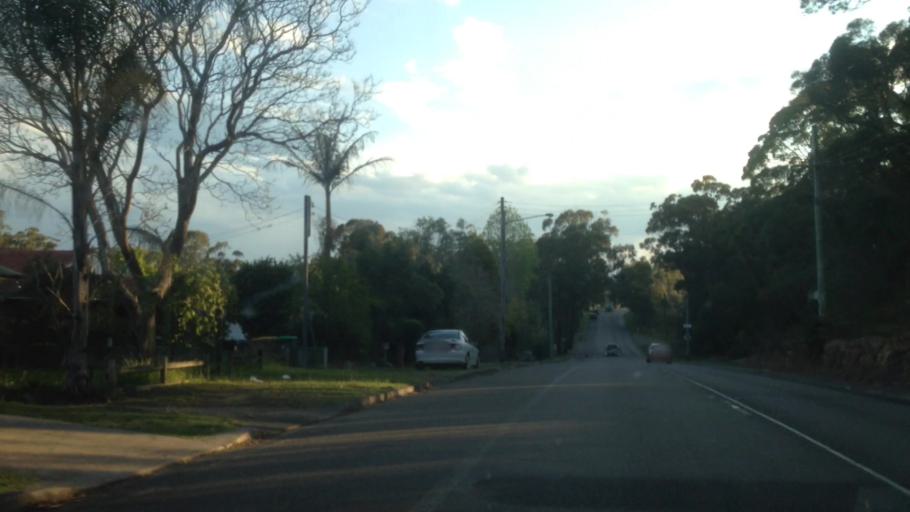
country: AU
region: New South Wales
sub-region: Lake Macquarie Shire
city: Cooranbong
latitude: -33.0647
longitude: 151.4696
